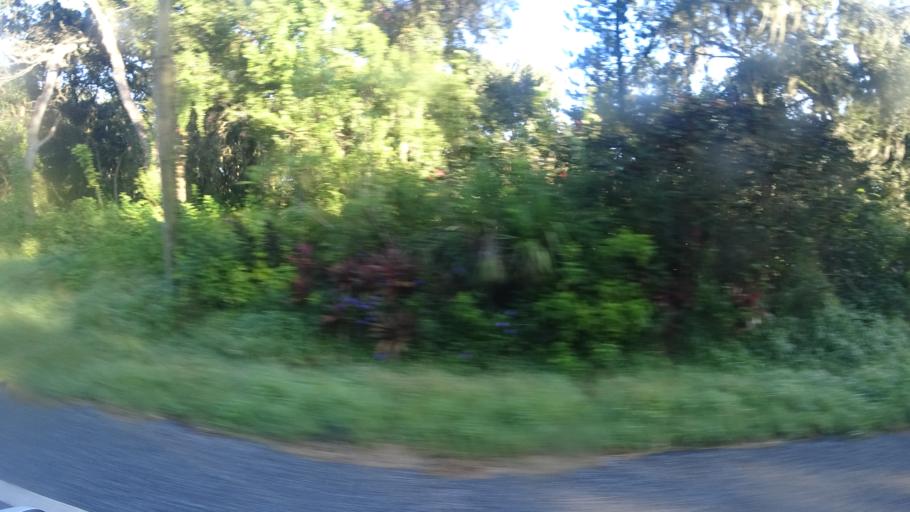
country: US
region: Florida
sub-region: Manatee County
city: Ellenton
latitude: 27.5485
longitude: -82.4435
